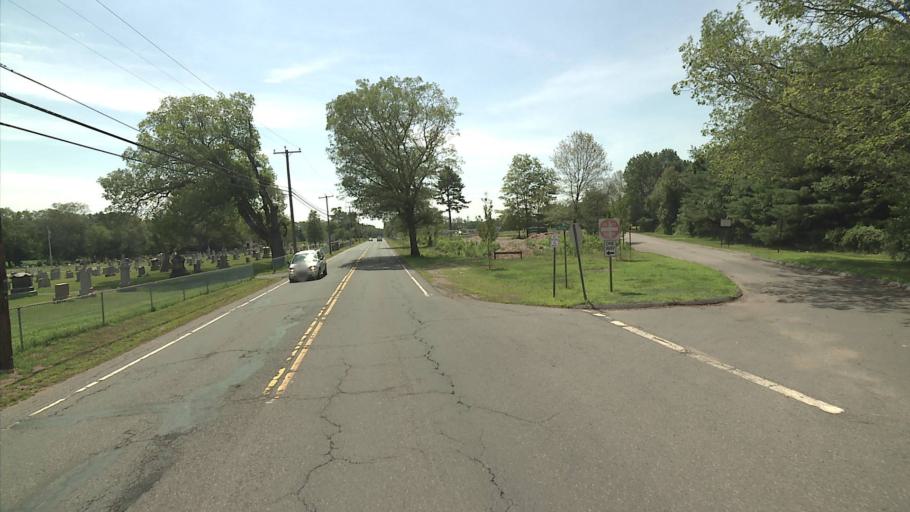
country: US
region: Connecticut
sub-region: Tolland County
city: South Coventry
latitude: 41.7564
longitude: -72.2735
